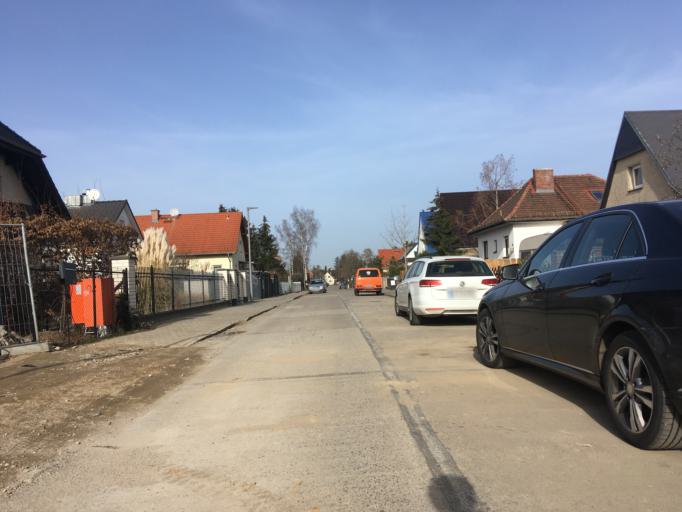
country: DE
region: Berlin
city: Bohnsdorf
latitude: 52.3951
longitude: 13.5682
